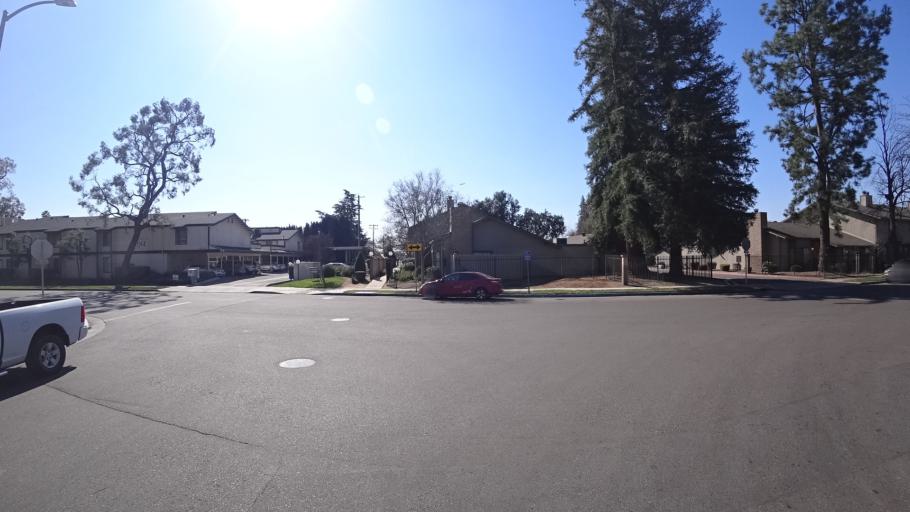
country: US
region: California
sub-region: Fresno County
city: Tarpey Village
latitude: 36.8056
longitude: -119.7408
